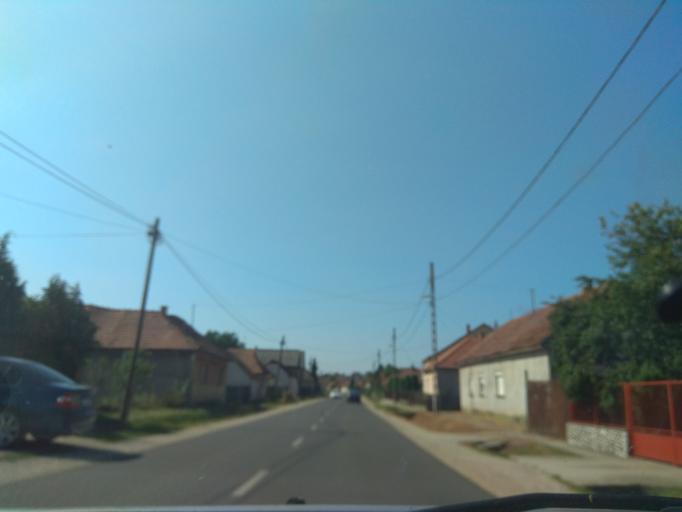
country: HU
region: Borsod-Abauj-Zemplen
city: Harsany
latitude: 47.9718
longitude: 20.7413
